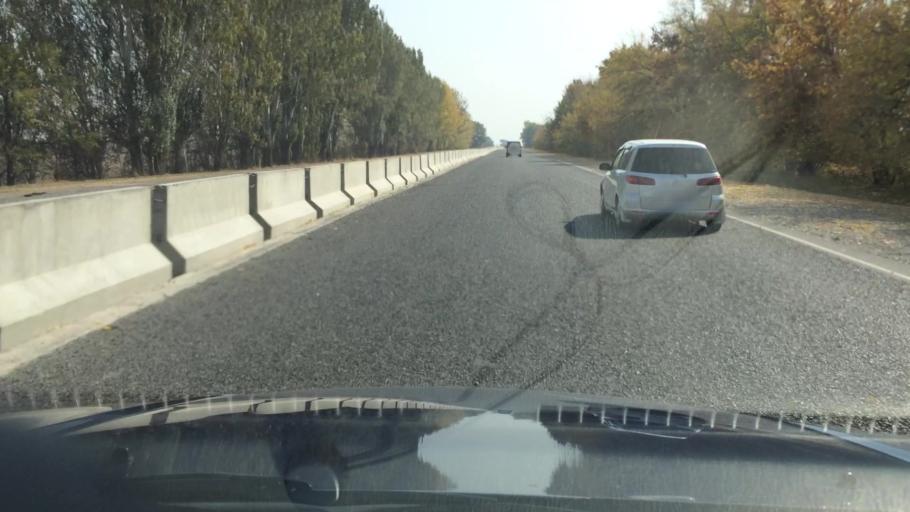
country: KG
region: Chuy
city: Kant
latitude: 42.9645
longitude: 74.9141
